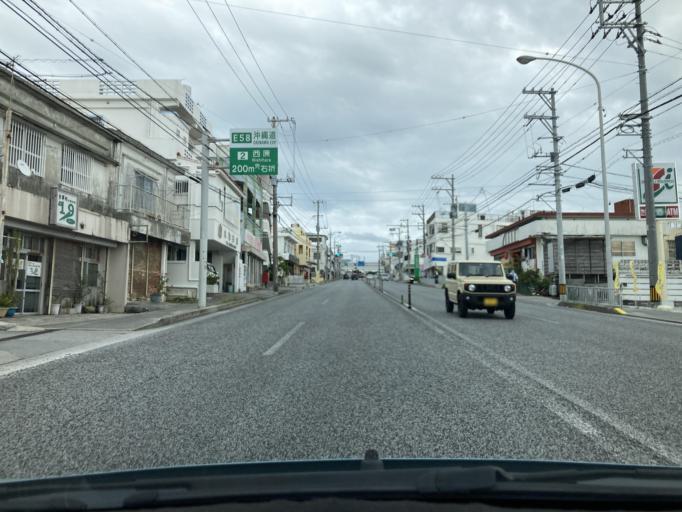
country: JP
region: Okinawa
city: Ginowan
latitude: 26.2572
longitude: 127.7512
